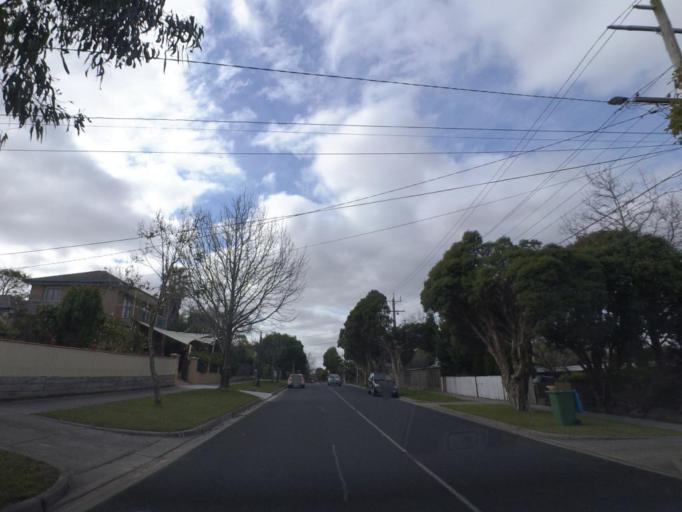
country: AU
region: Victoria
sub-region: Maroondah
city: Ringwood East
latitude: -37.7975
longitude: 145.2440
